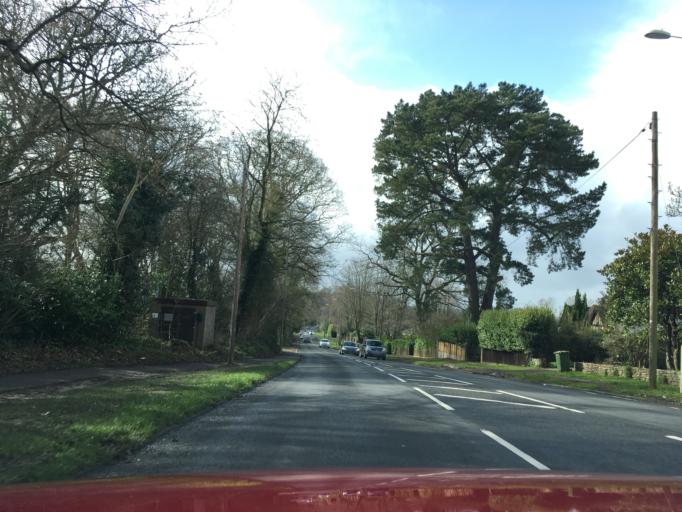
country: GB
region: England
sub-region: Hampshire
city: Chandlers Ford
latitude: 50.9938
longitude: -1.3655
